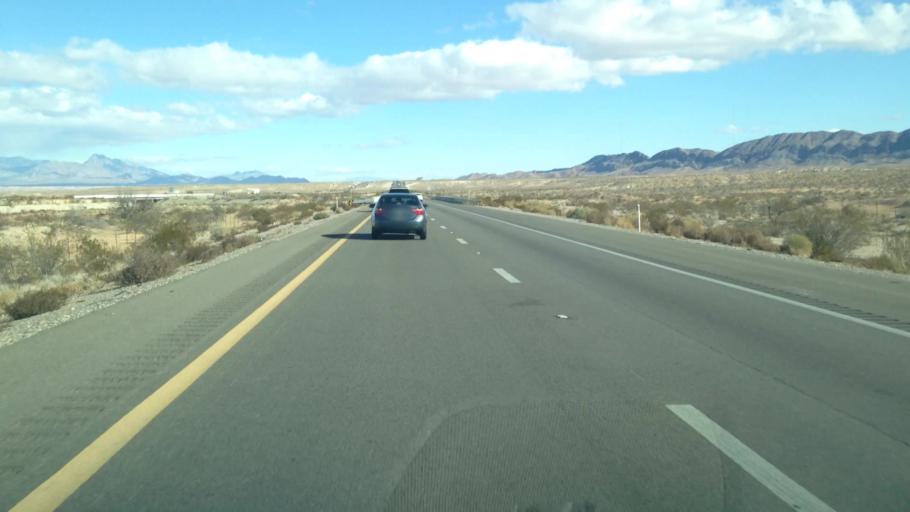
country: US
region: Nevada
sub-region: Clark County
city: Moapa Town
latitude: 36.5560
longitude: -114.6910
